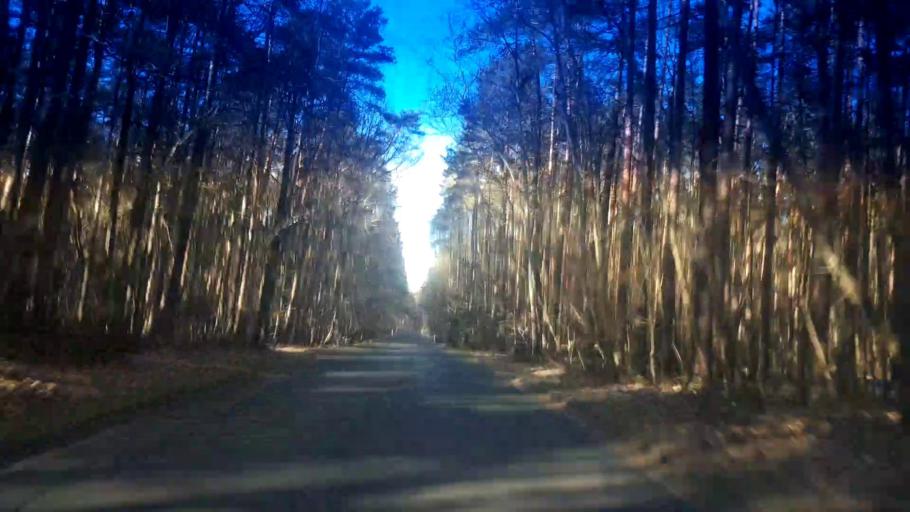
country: DE
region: Bavaria
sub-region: Upper Franconia
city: Lauter
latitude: 49.9590
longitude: 10.7616
